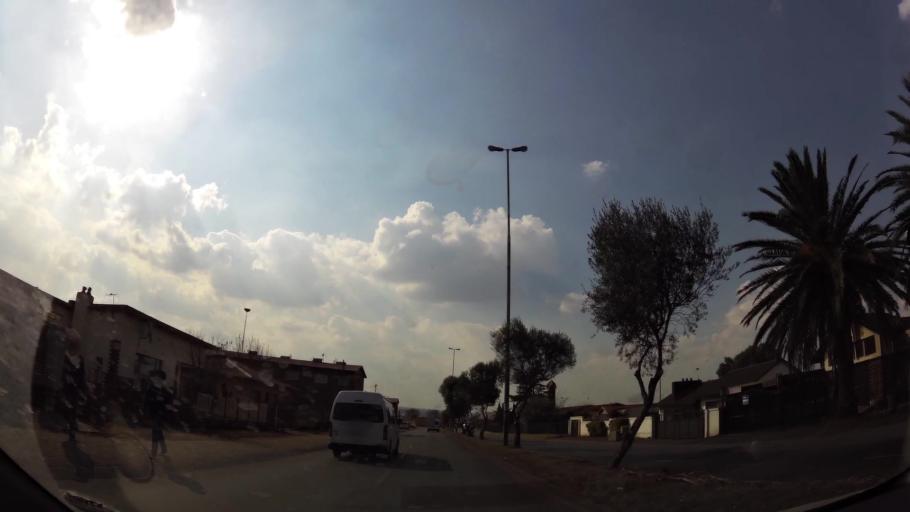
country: ZA
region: Gauteng
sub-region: Ekurhuleni Metropolitan Municipality
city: Germiston
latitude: -26.3153
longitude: 28.1514
